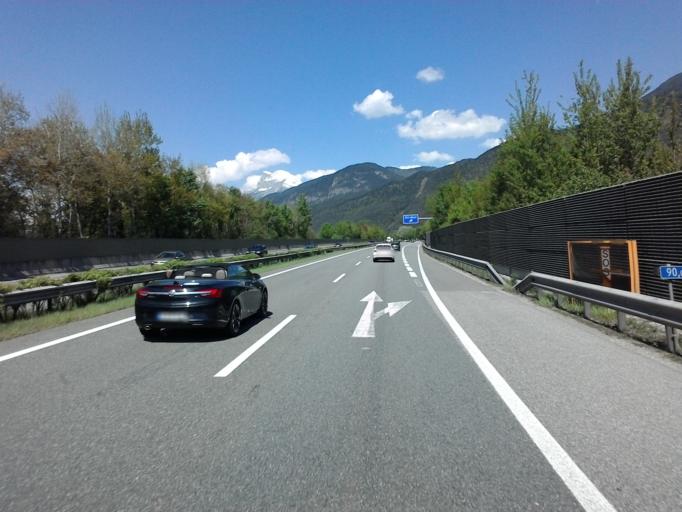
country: AT
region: Tyrol
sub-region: Politischer Bezirk Innsbruck Land
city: Unterperfuss
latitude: 47.2661
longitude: 11.2332
